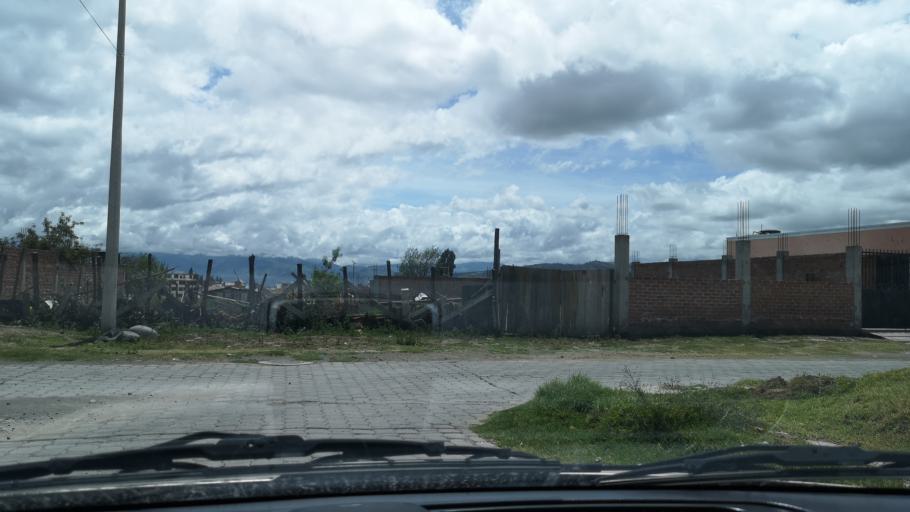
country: EC
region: Chimborazo
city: Riobamba
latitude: -1.6417
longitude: -78.6837
